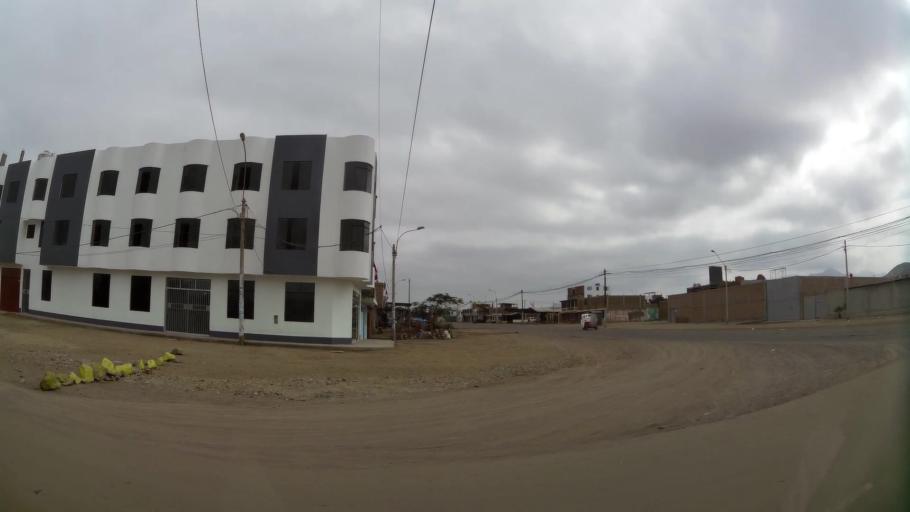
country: PE
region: Lima
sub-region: Provincia de Canete
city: Chilca
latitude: -12.5190
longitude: -76.7321
